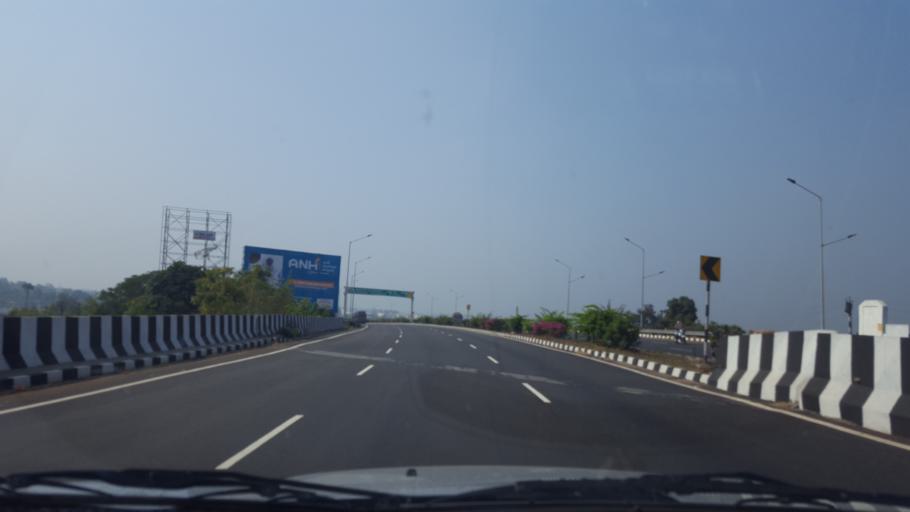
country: IN
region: Andhra Pradesh
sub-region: Vishakhapatnam
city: Bhimunipatnam
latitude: 17.9617
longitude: 83.4196
